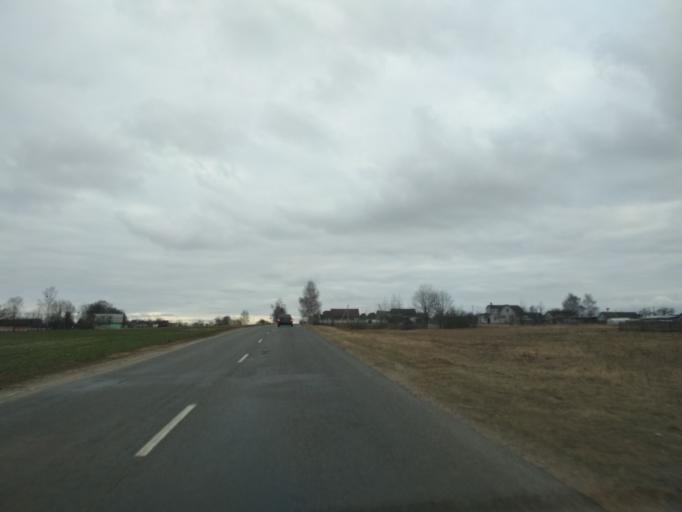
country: BY
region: Minsk
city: Svislach
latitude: 53.5690
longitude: 28.0030
